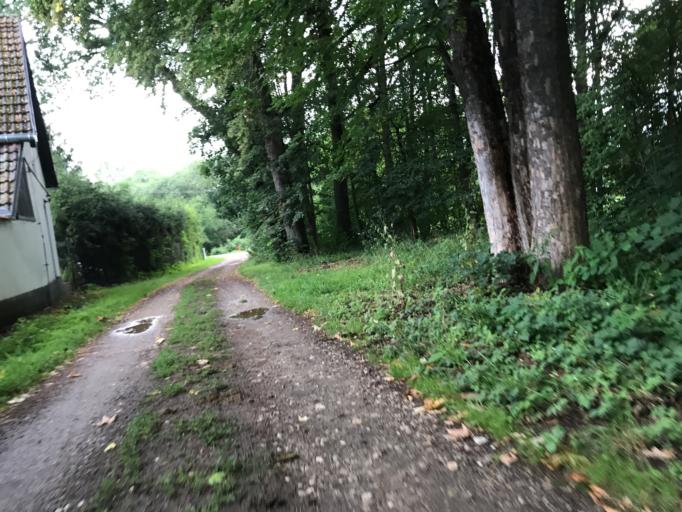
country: CZ
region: Jihocesky
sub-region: Okres Jindrichuv Hradec
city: Trebon
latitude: 48.9890
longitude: 14.7804
